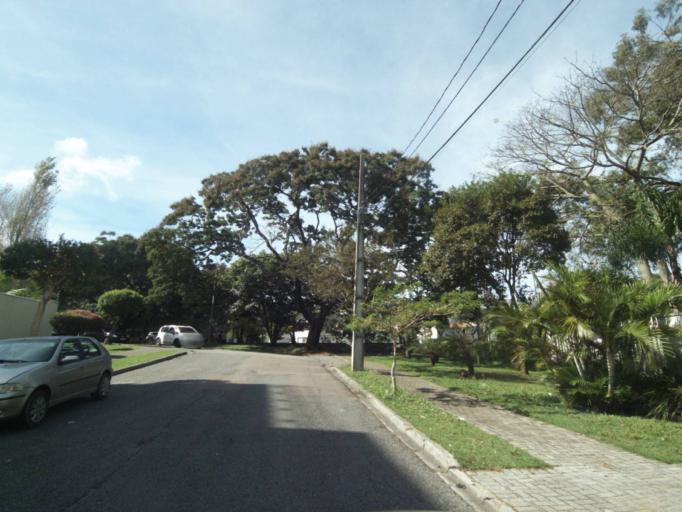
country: BR
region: Parana
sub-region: Curitiba
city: Curitiba
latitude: -25.4215
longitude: -49.2464
